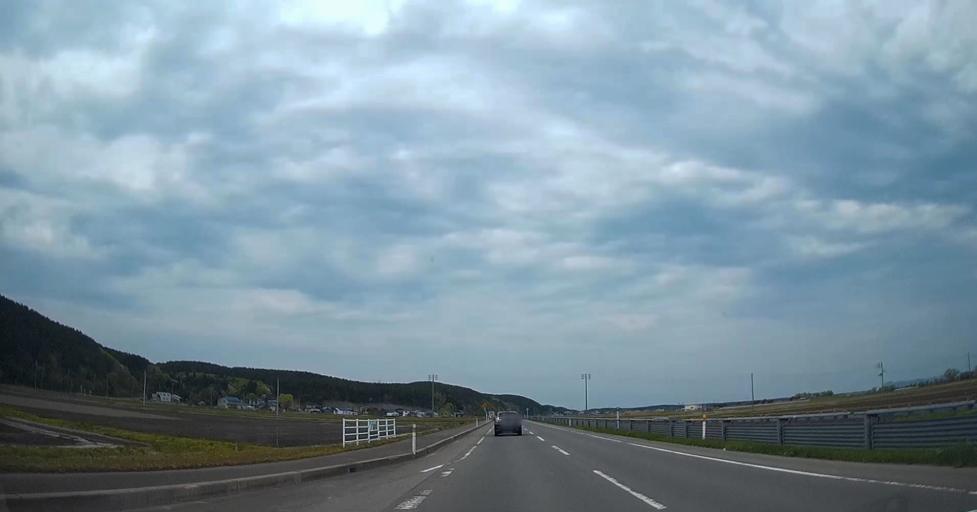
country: JP
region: Aomori
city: Shimokizukuri
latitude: 40.9926
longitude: 140.3632
